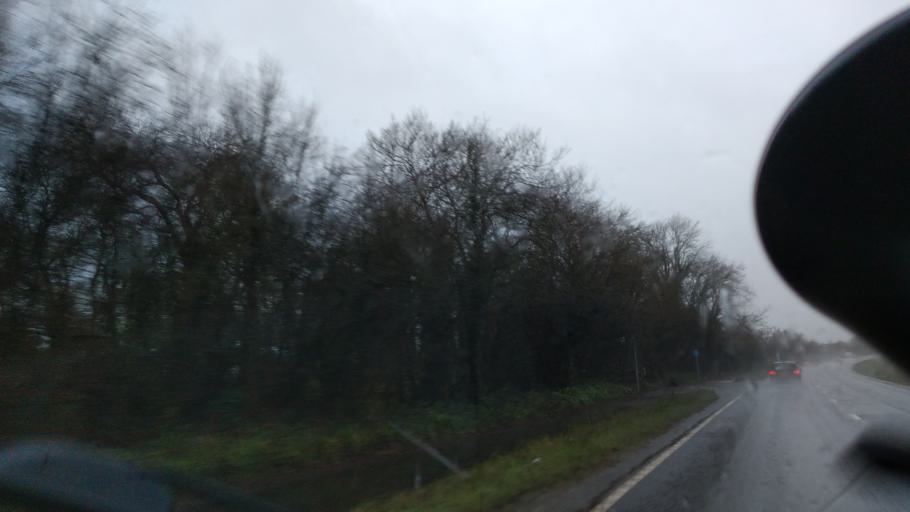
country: GB
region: England
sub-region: West Sussex
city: Rustington
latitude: 50.8410
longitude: -0.4961
